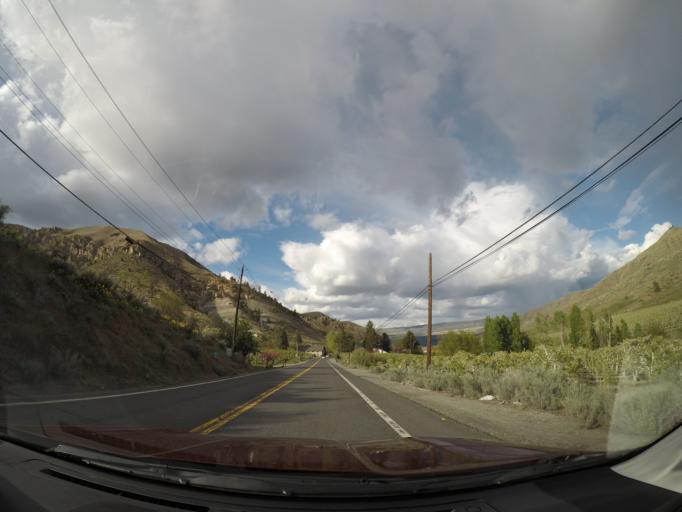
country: US
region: Washington
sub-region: Chelan County
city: South Wenatchee
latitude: 47.3723
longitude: -120.3227
